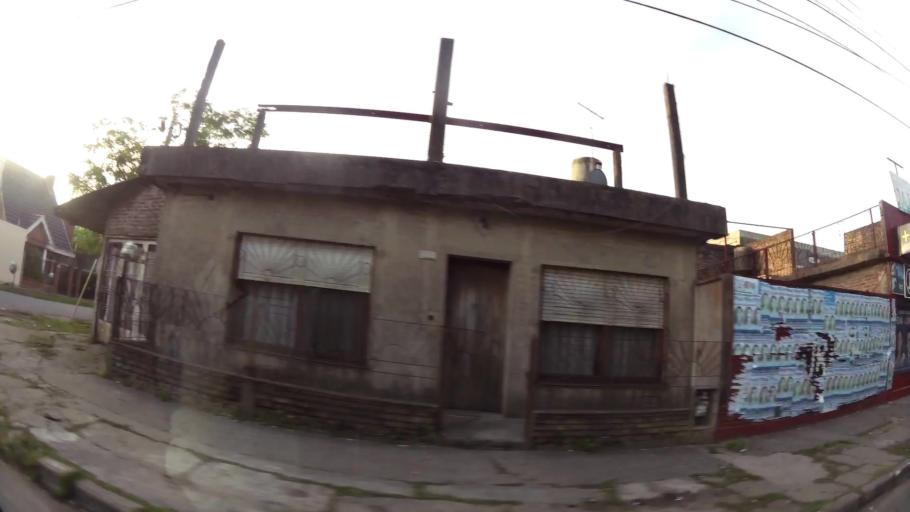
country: AR
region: Buenos Aires
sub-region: Partido de Quilmes
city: Quilmes
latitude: -34.7807
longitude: -58.2122
